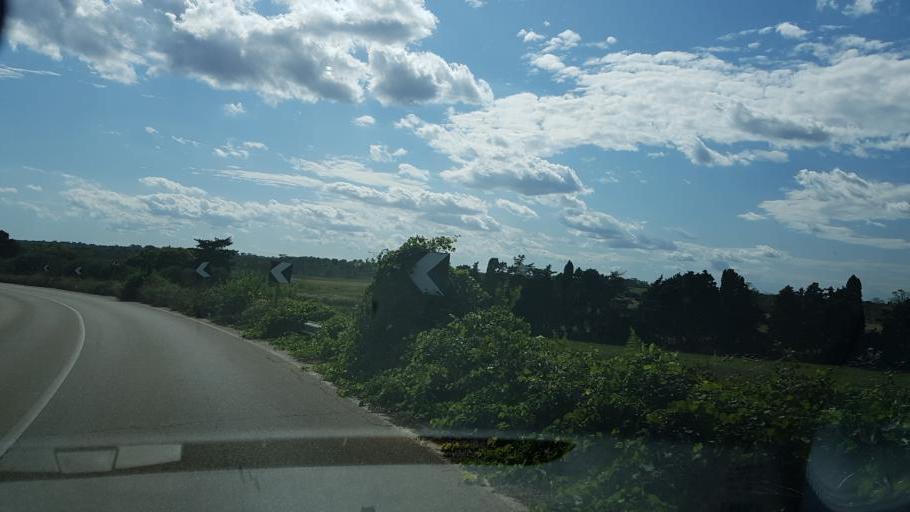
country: IT
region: Apulia
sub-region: Provincia di Lecce
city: Borgagne
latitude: 40.2248
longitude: 18.4412
